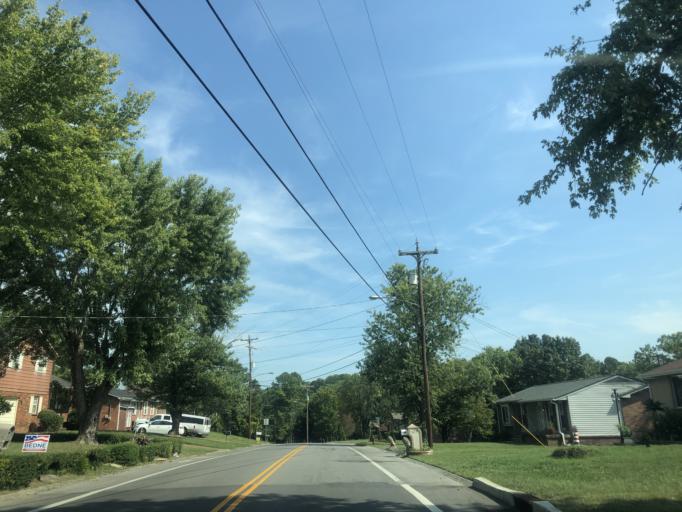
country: US
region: Tennessee
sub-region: Williamson County
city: Brentwood Estates
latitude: 36.0521
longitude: -86.7059
